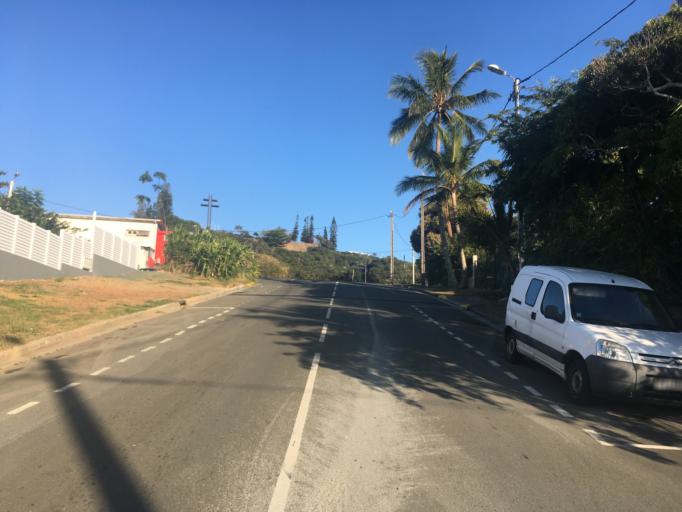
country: NC
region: South Province
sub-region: Noumea
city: Noumea
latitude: -22.2794
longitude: 166.4496
